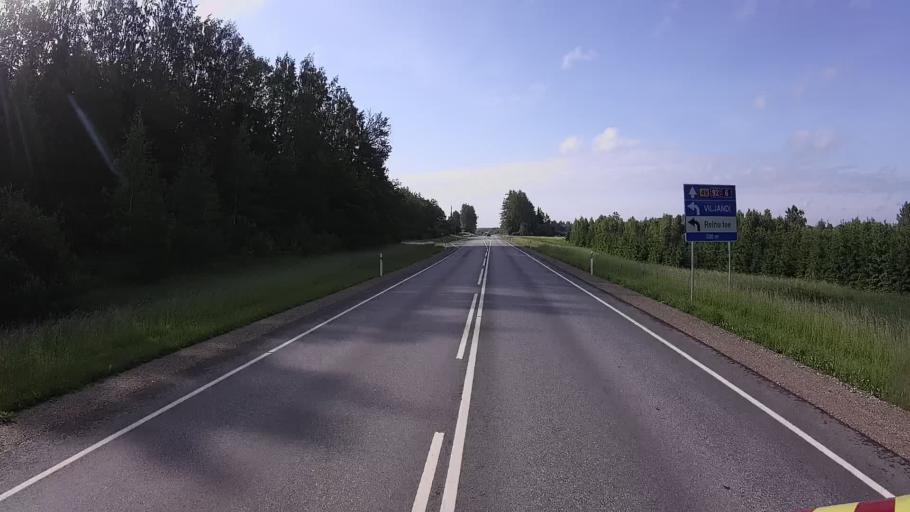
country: EE
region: Viljandimaa
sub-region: Viljandi linn
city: Viljandi
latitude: 58.3481
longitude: 25.5634
